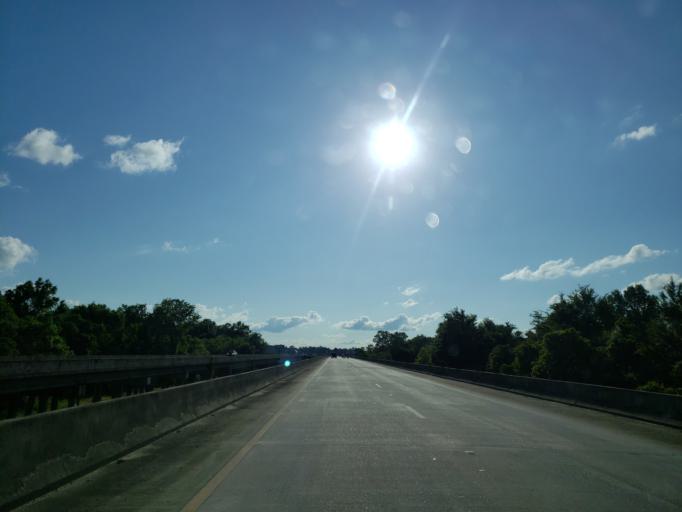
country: US
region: Mississippi
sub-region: Forrest County
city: Petal
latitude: 31.3597
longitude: -89.2806
